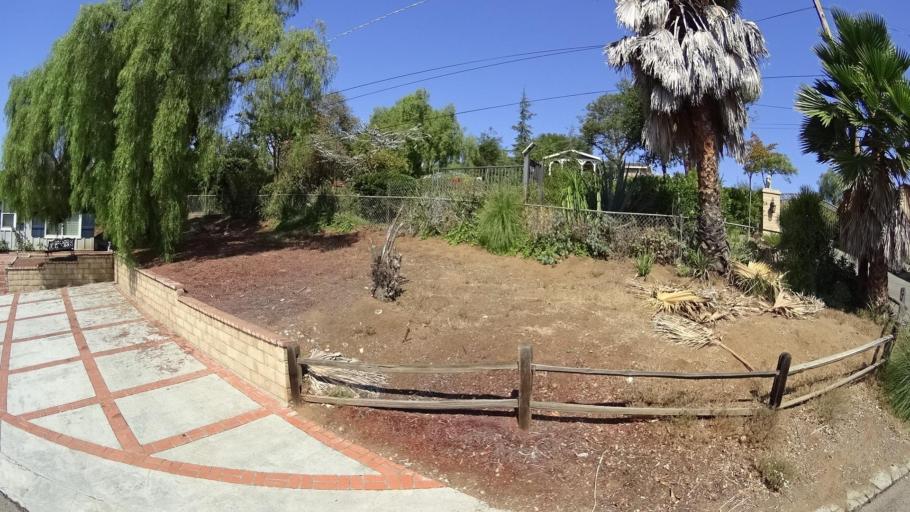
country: US
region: California
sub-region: San Diego County
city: Vista
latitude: 33.1789
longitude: -117.2125
